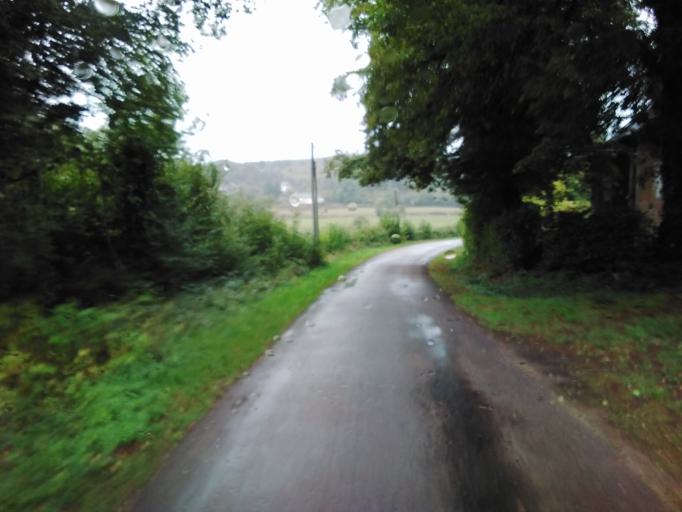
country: FR
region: Bourgogne
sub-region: Departement de la Nievre
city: Lormes
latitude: 47.2918
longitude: 3.9722
